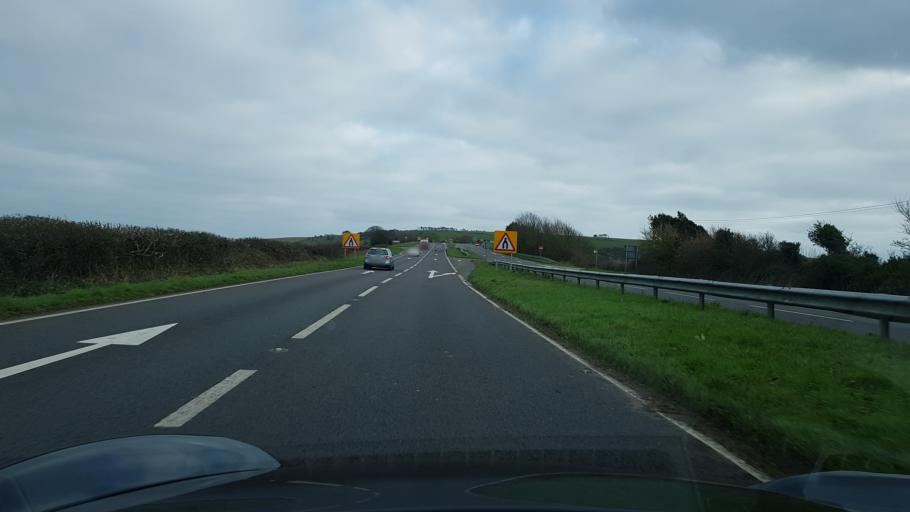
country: GB
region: England
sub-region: Dorset
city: Bridport
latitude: 50.7303
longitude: -2.6815
